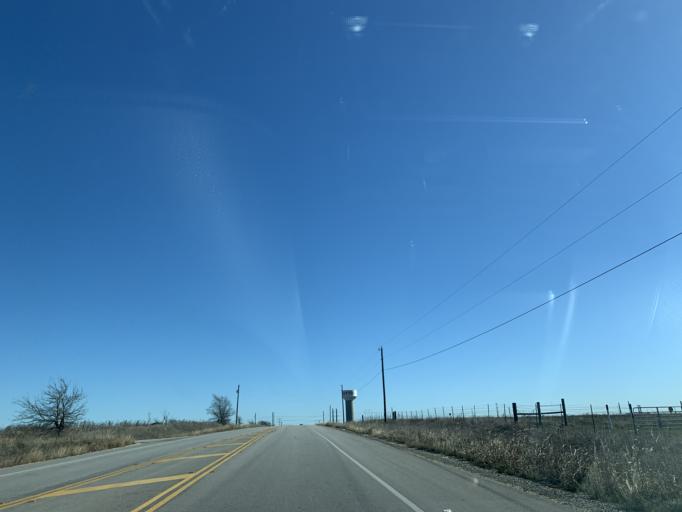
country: US
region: Texas
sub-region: Williamson County
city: Hutto
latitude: 30.5584
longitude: -97.5686
